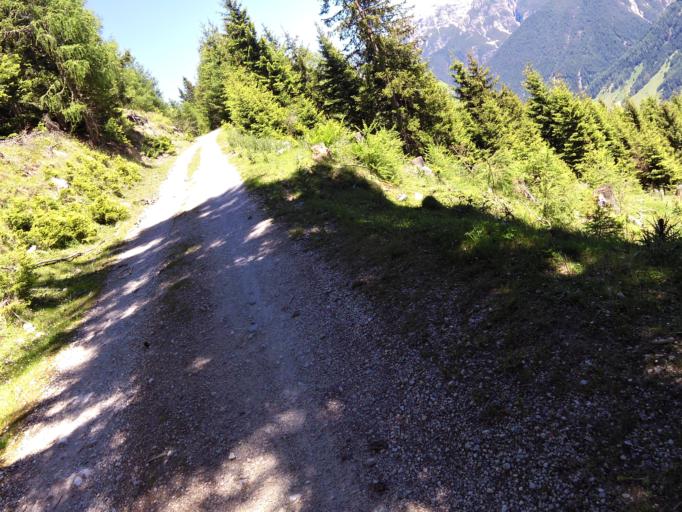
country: AT
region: Tyrol
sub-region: Politischer Bezirk Innsbruck Land
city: Neustift im Stubaital
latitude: 47.1142
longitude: 11.2869
